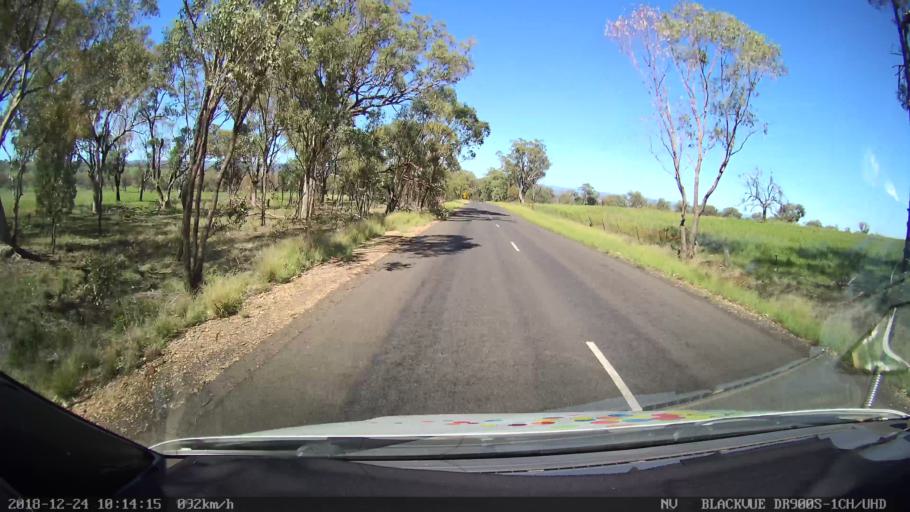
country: AU
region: New South Wales
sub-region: Liverpool Plains
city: Quirindi
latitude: -31.6962
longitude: 150.6306
